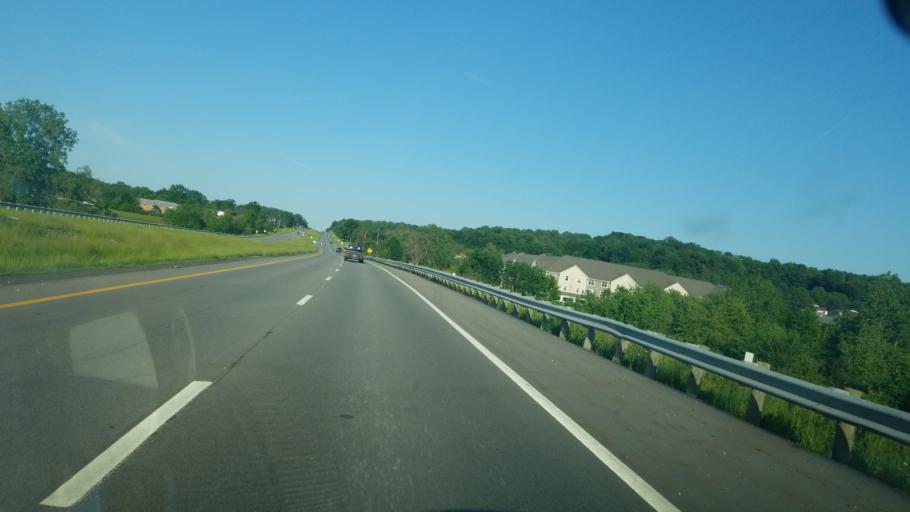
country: US
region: Ohio
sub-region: Portage County
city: Kent
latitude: 41.1344
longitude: -81.3674
